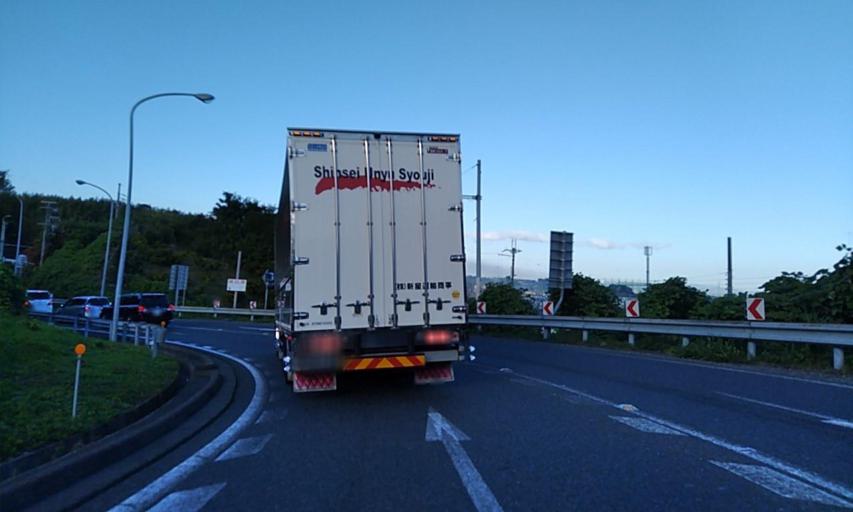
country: JP
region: Wakayama
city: Iwade
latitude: 34.3472
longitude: 135.2756
